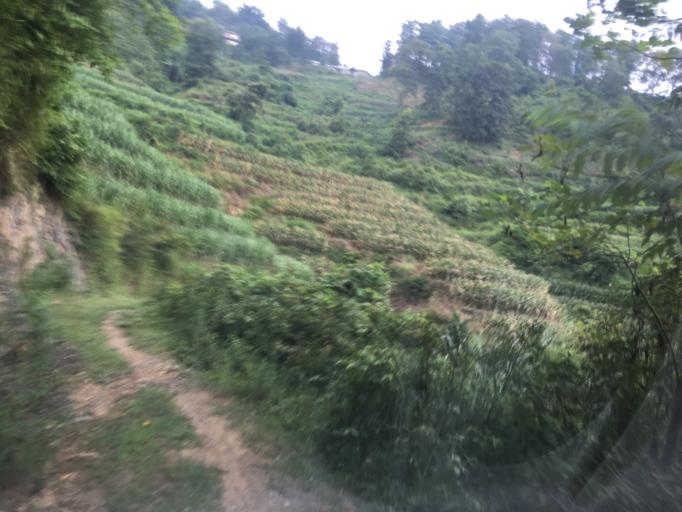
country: CN
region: Guangxi Zhuangzu Zizhiqu
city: Xinzhou
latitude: 25.1677
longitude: 105.6991
